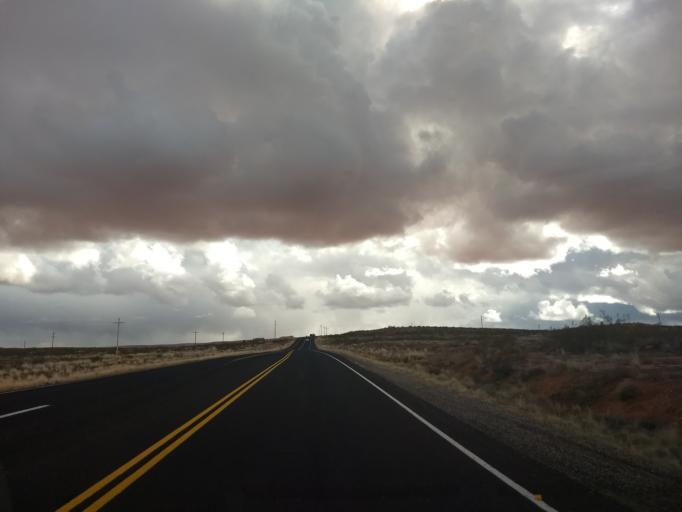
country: US
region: Utah
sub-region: Washington County
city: Hurricane
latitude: 37.1446
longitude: -113.3897
